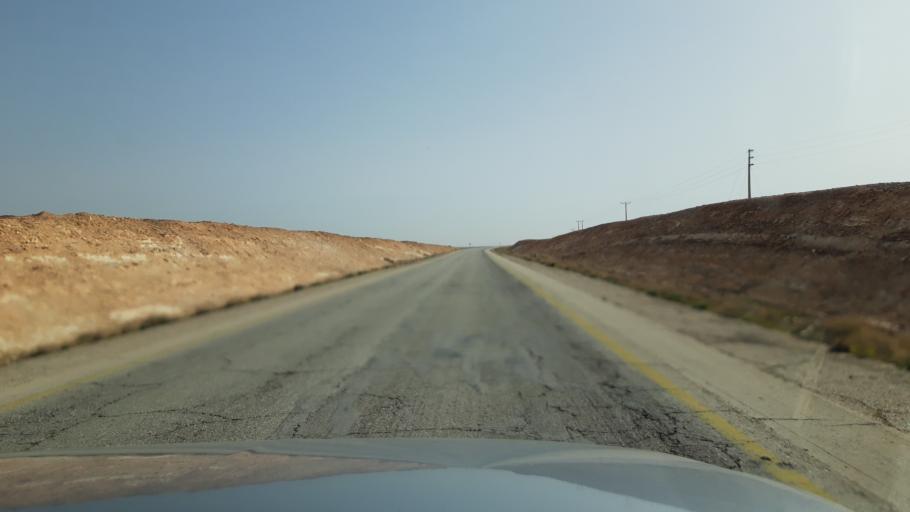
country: JO
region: Amman
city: Al Azraq ash Shamali
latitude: 31.8630
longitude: 36.7059
